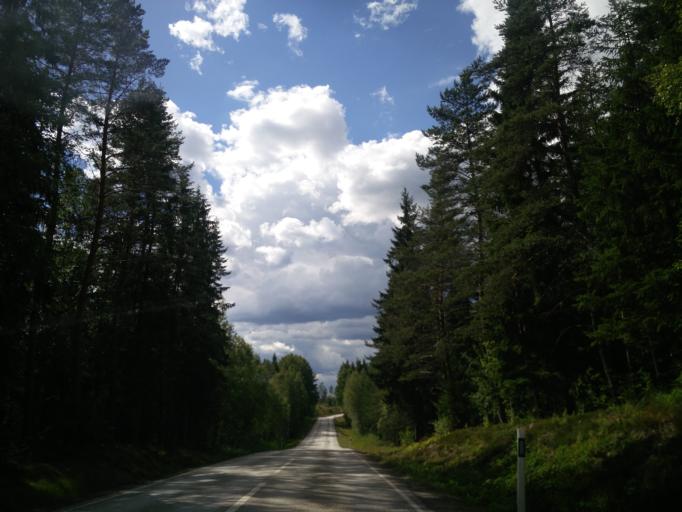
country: SE
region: OErebro
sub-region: Hallefors Kommun
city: Haellefors
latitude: 59.8024
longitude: 14.7176
